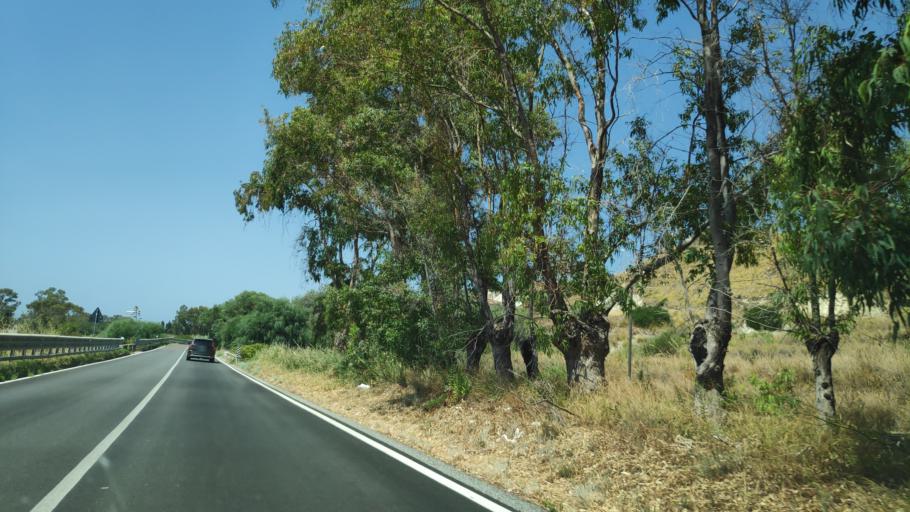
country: IT
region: Calabria
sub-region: Provincia di Reggio Calabria
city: Weather Station
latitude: 37.9246
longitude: 16.0539
